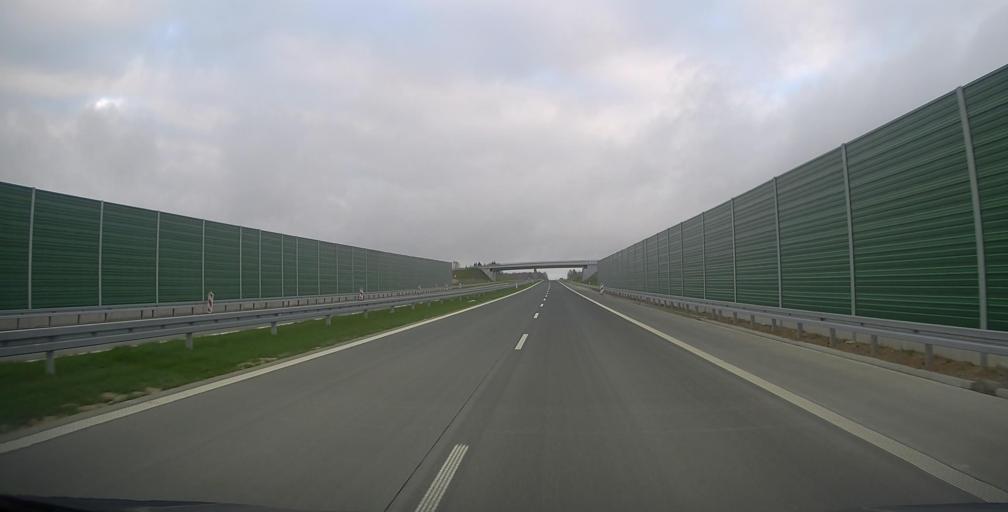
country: PL
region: Podlasie
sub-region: Powiat suwalski
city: Raczki
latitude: 53.9399
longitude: 22.7624
